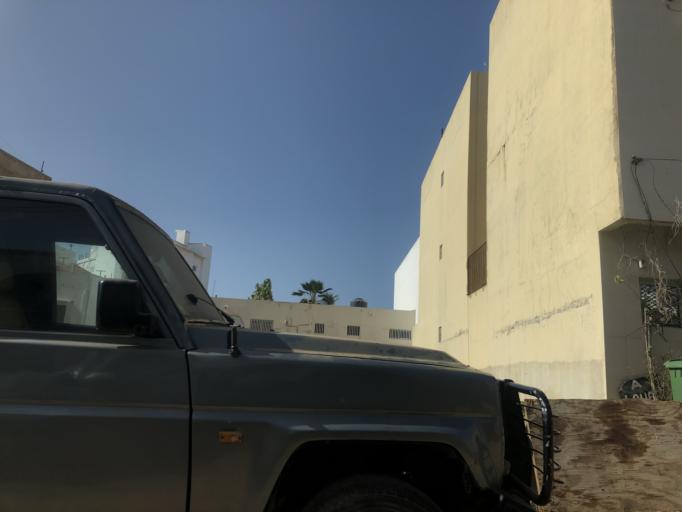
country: SN
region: Dakar
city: Mermoz Boabab
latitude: 14.7558
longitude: -17.4911
